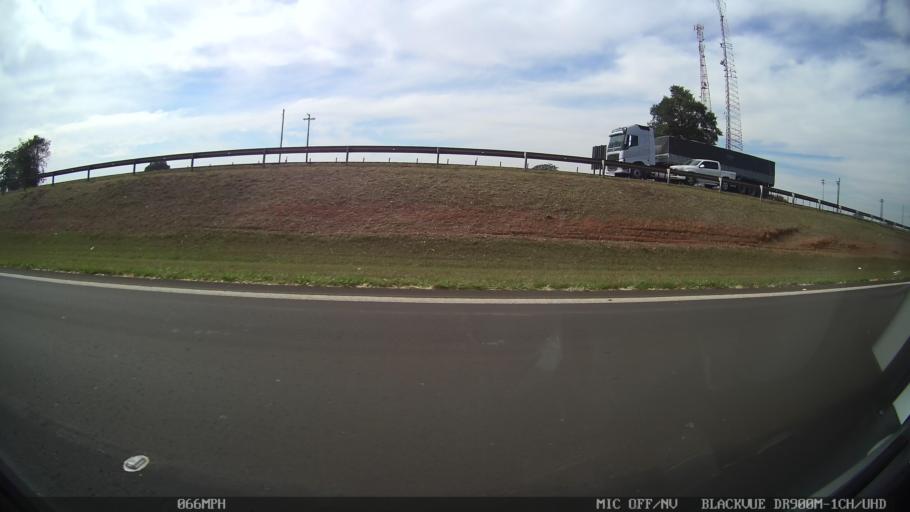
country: BR
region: Sao Paulo
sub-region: Matao
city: Matao
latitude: -21.5975
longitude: -48.4361
